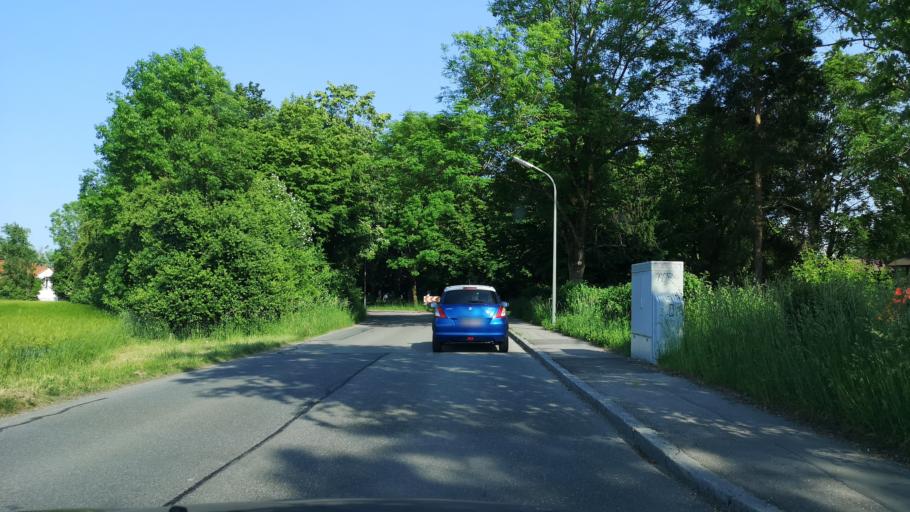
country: DE
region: Bavaria
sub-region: Upper Bavaria
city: Kirchheim bei Muenchen
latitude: 48.1714
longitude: 11.7758
